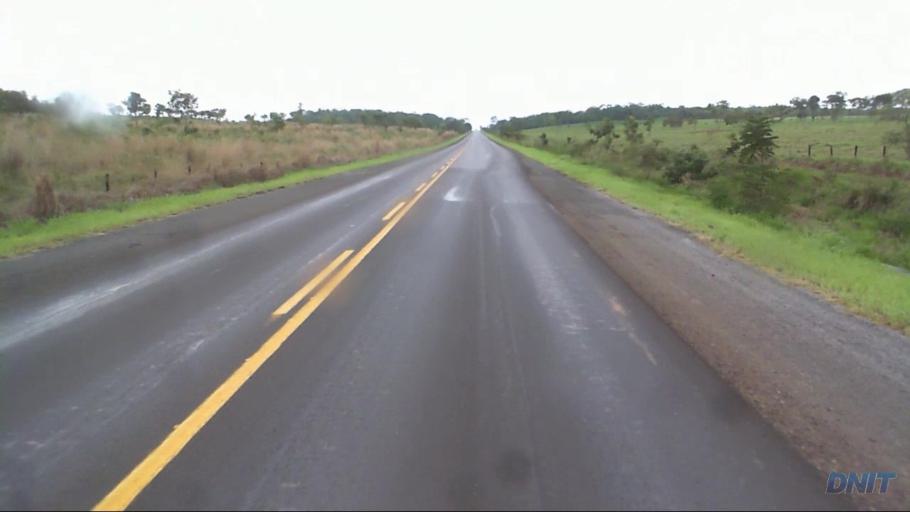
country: BR
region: Goias
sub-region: Padre Bernardo
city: Padre Bernardo
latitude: -15.2083
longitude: -48.4691
